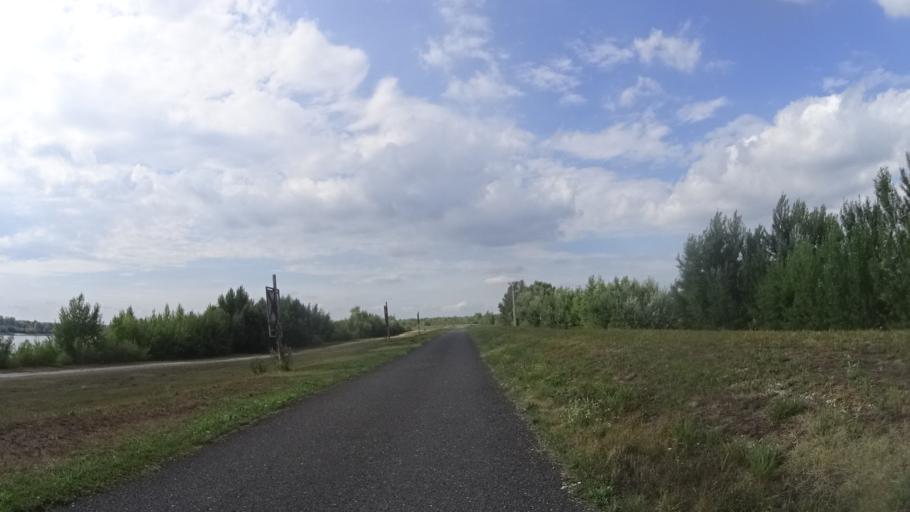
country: SK
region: Trnavsky
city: Gabcikovo
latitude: 47.8708
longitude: 17.5555
